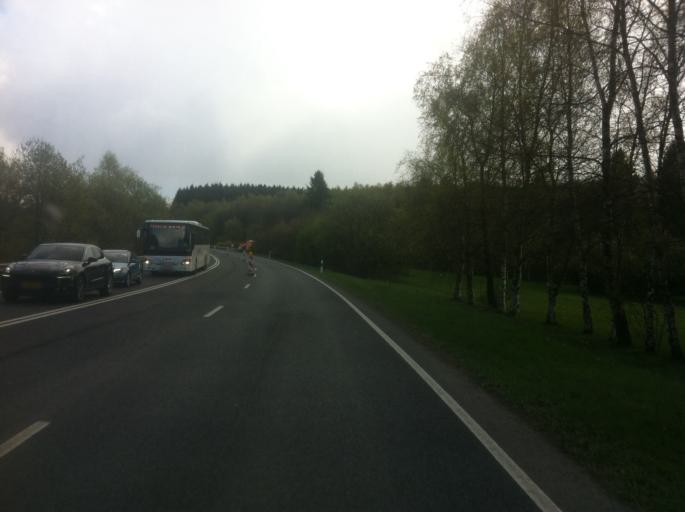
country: LU
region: Diekirch
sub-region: Canton de Wiltz
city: Winseler
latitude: 49.9583
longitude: 5.8613
